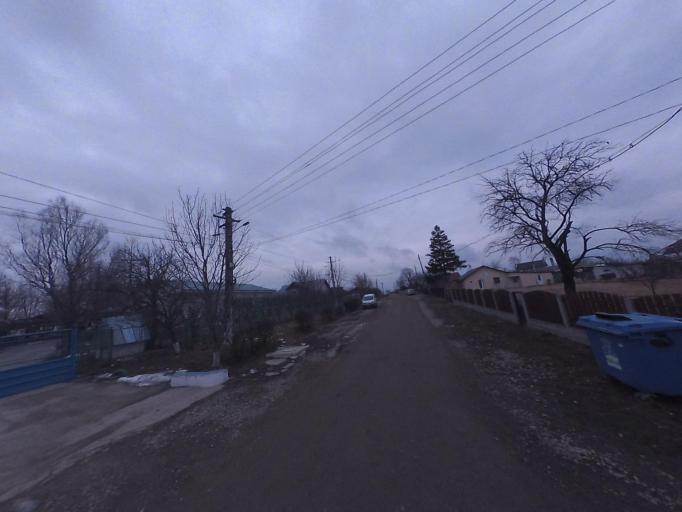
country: RO
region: Iasi
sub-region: Comuna Popricani
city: Popricani
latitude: 47.2915
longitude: 27.5051
